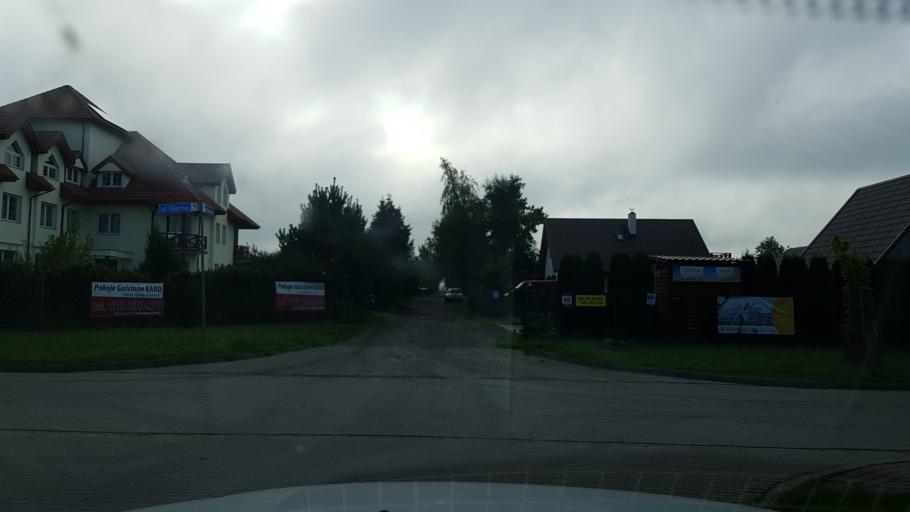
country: PL
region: West Pomeranian Voivodeship
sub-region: Powiat kolobrzeski
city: Ustronie Morskie
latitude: 54.2124
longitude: 15.7555
